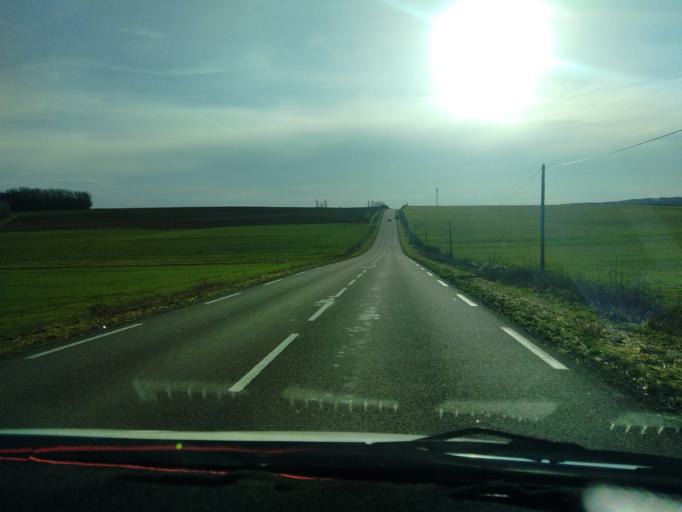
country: FR
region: Franche-Comte
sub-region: Departement de la Haute-Saone
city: Gray
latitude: 47.3999
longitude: 5.6446
